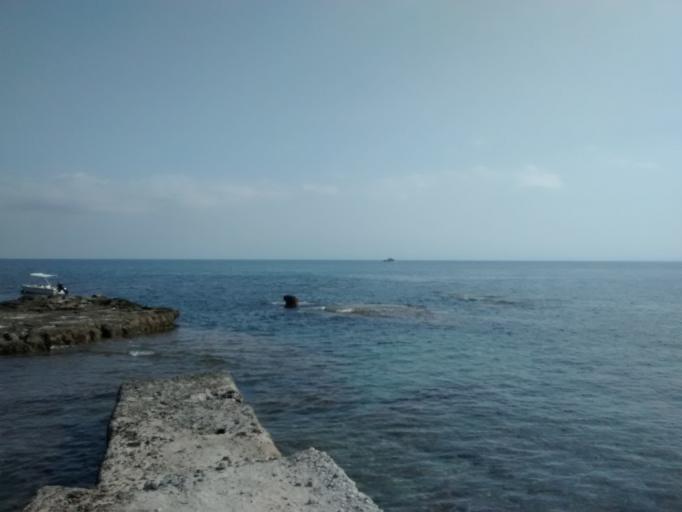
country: IT
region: Calabria
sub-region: Provincia di Vibo-Valentia
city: Briatico
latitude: 38.7262
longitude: 16.0430
